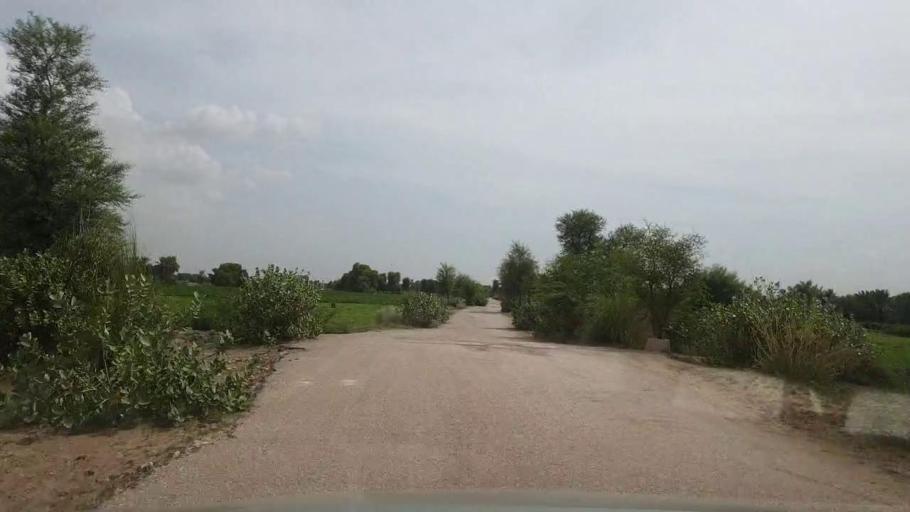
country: PK
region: Sindh
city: Kot Diji
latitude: 27.1185
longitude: 69.0251
